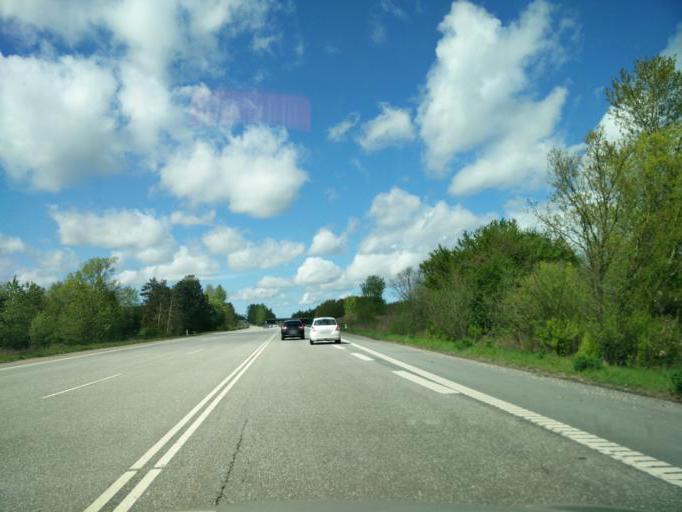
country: DK
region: Capital Region
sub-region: Allerod Kommune
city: Lillerod
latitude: 55.8595
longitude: 12.3205
